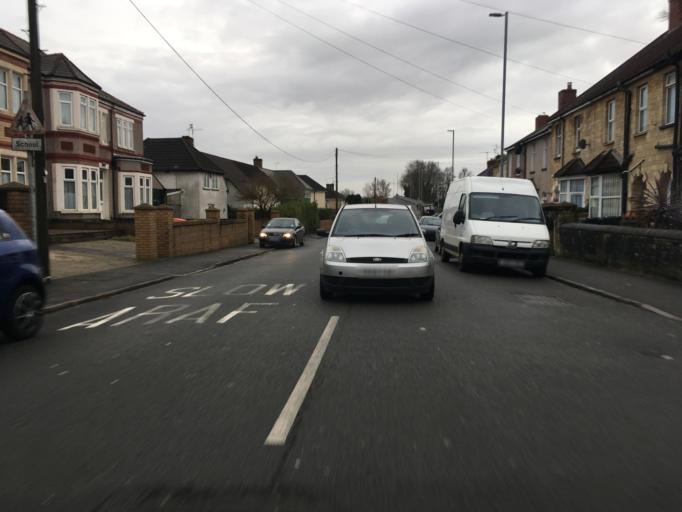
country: GB
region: Wales
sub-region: Newport
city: Caerleon
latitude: 51.5871
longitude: -2.9627
